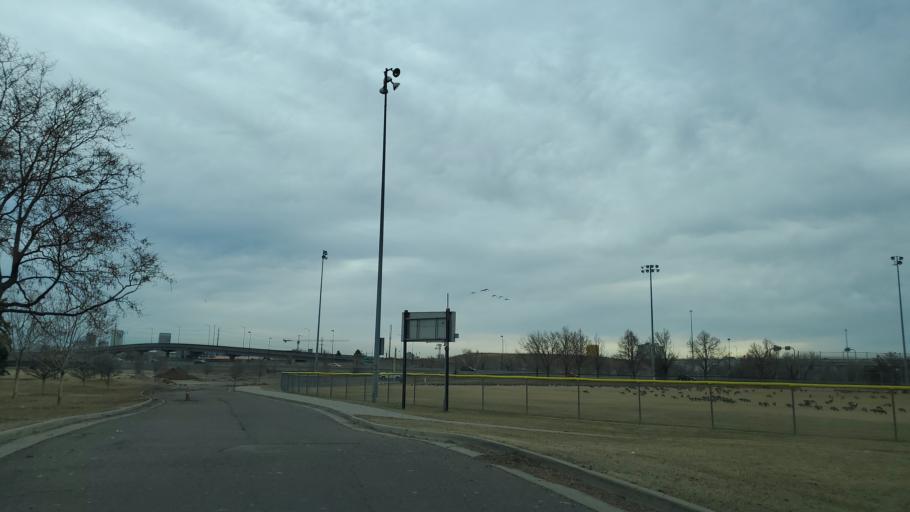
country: US
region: Colorado
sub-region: Denver County
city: Denver
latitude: 39.7007
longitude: -104.9966
